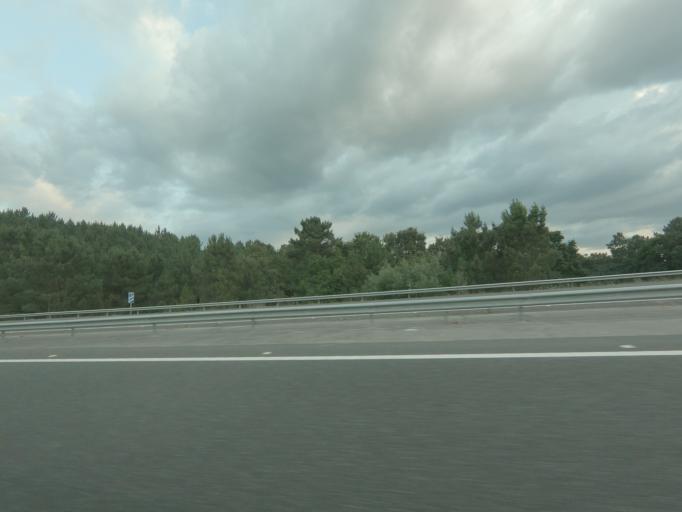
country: ES
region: Galicia
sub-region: Provincia de Ourense
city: Punxin
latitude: 42.3417
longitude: -8.0010
